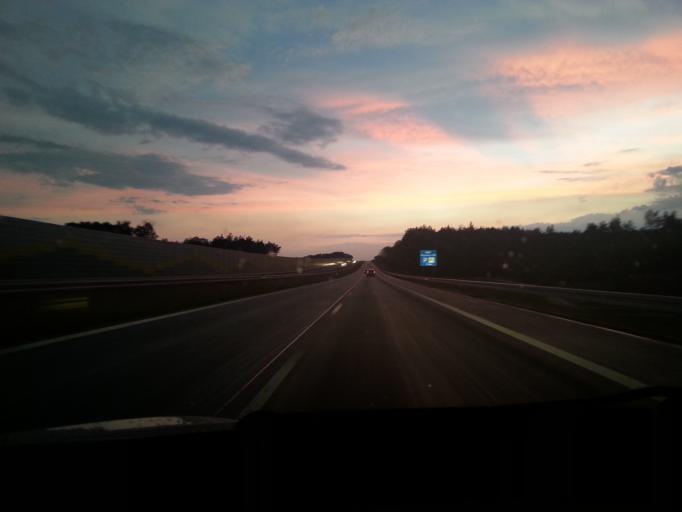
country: PL
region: Lodz Voivodeship
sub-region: Powiat zdunskowolski
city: Zdunska Wola
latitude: 51.5688
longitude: 18.9727
